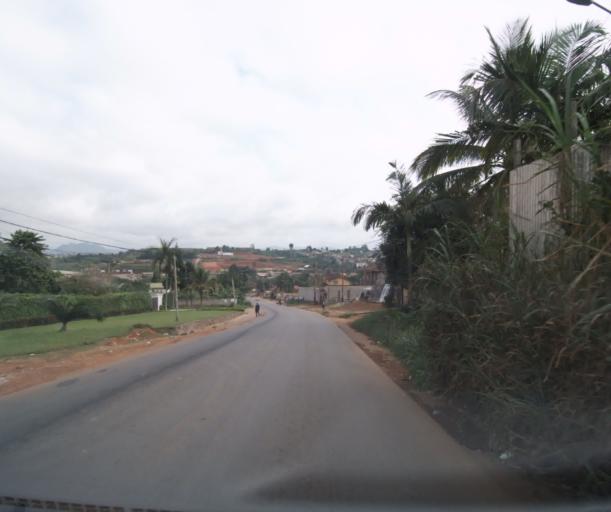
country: CM
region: Centre
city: Yaounde
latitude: 3.8036
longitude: 11.5221
